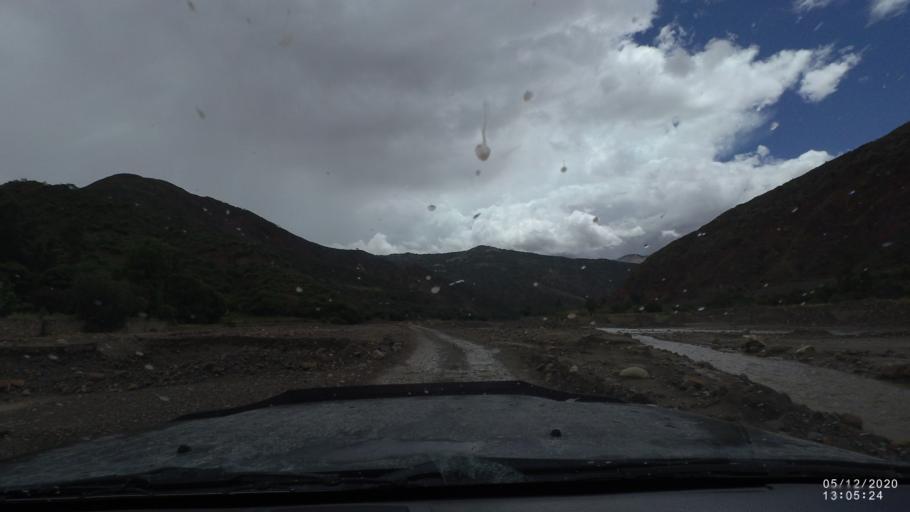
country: BO
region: Cochabamba
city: Sipe Sipe
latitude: -17.5543
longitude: -66.4421
